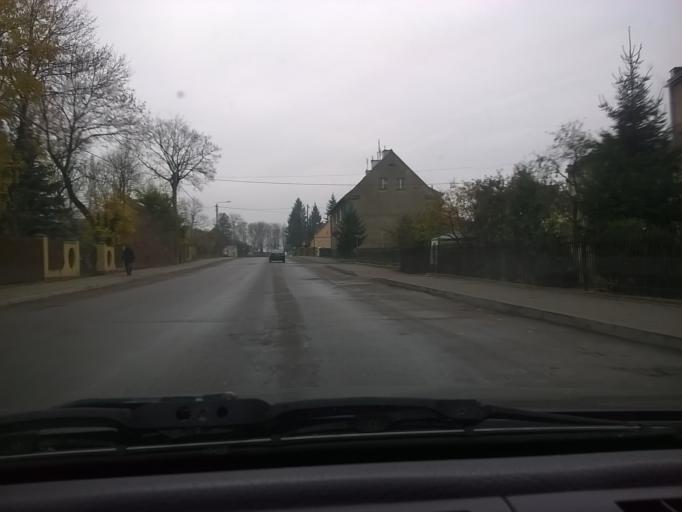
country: PL
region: Warmian-Masurian Voivodeship
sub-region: Powiat ketrzynski
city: Ketrzyn
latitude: 54.0694
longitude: 21.3762
